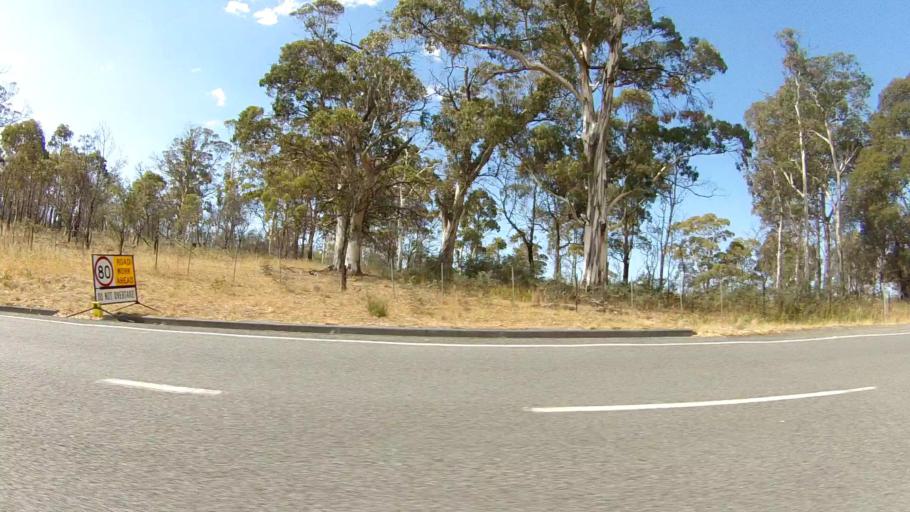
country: AU
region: Tasmania
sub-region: Sorell
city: Sorell
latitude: -42.6118
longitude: 147.6466
